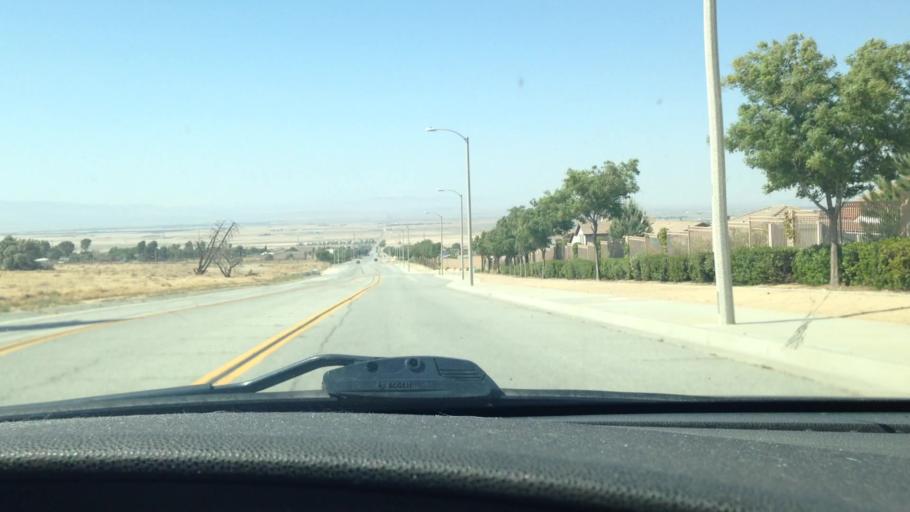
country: US
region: California
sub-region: Los Angeles County
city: Quartz Hill
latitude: 34.6388
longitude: -118.2535
